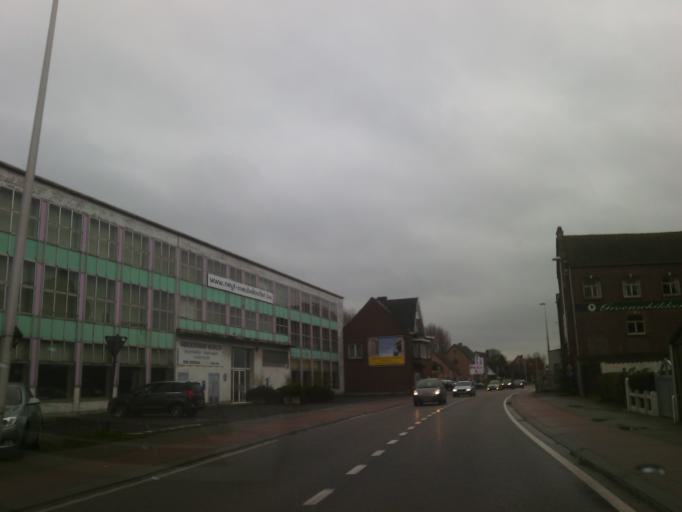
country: BE
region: Flanders
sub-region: Provincie Oost-Vlaanderen
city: Lochristi
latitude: 51.0793
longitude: 3.8808
